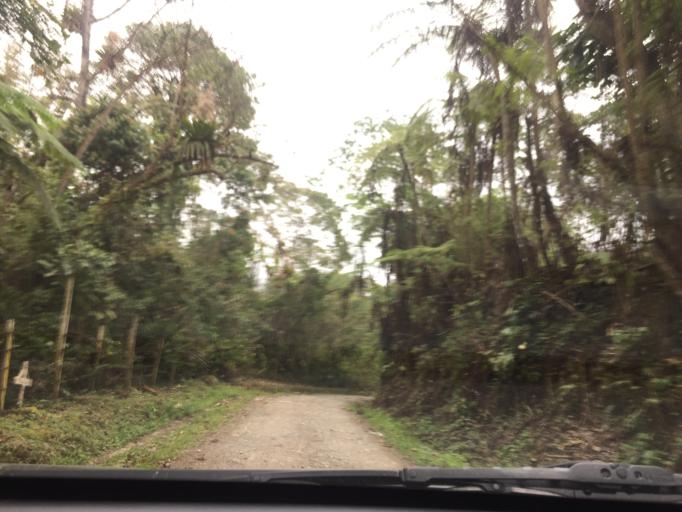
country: CO
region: Cundinamarca
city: Bojaca
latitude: 4.6882
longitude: -74.3737
